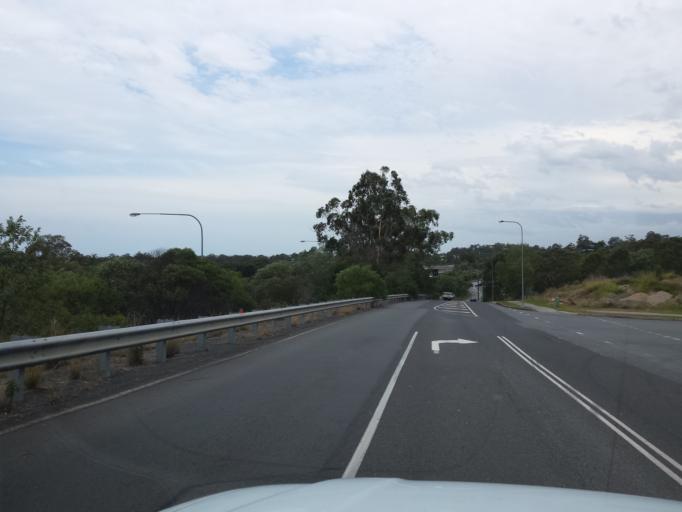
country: AU
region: Queensland
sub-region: Gold Coast
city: Nerang
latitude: -28.0117
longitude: 153.3457
